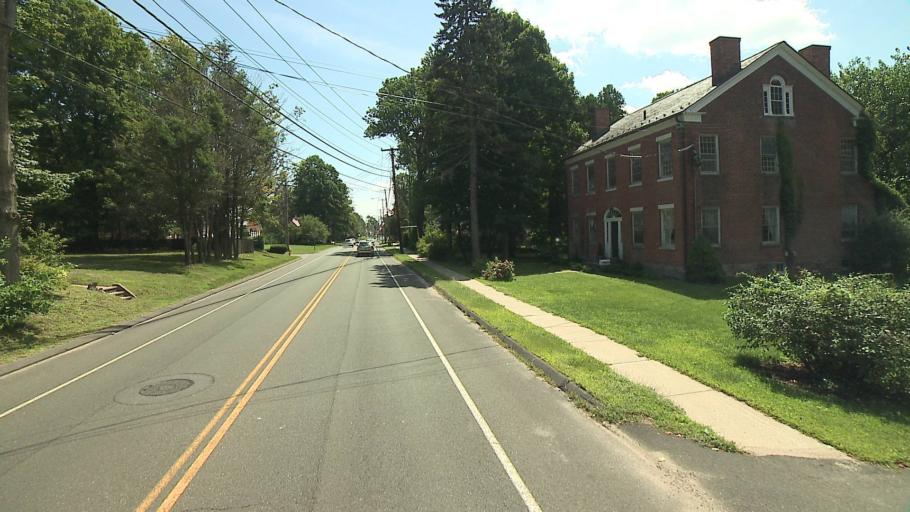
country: US
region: Connecticut
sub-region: Fairfield County
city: Trumbull
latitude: 41.2635
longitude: -73.2227
